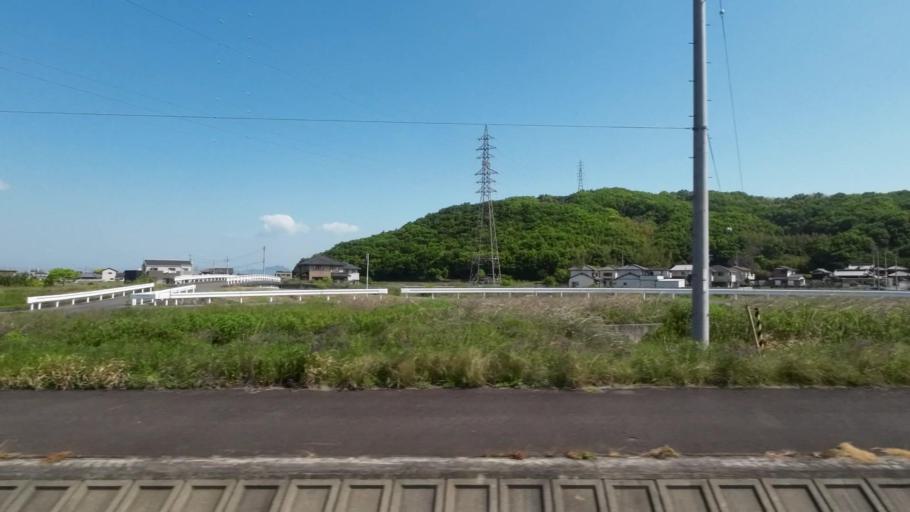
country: JP
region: Kagawa
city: Tadotsu
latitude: 34.2522
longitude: 133.7367
